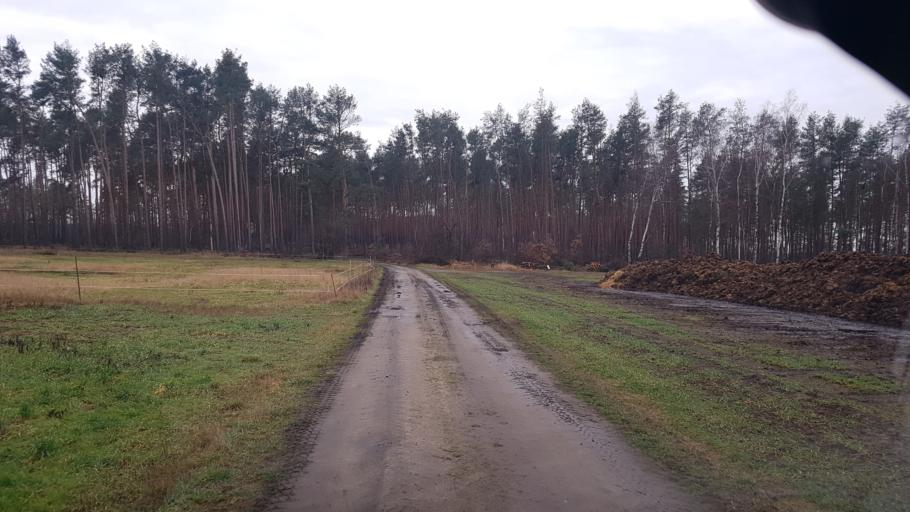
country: DE
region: Brandenburg
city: Schonborn
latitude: 51.5519
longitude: 13.4641
